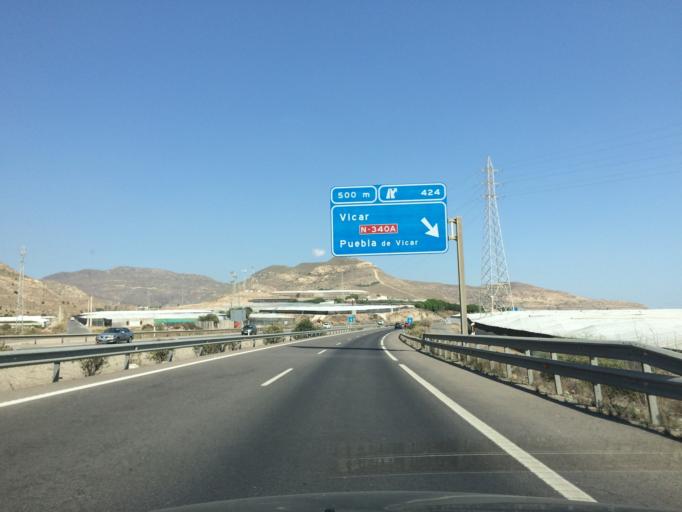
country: ES
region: Andalusia
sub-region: Provincia de Almeria
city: Vicar
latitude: 36.8117
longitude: -2.6631
